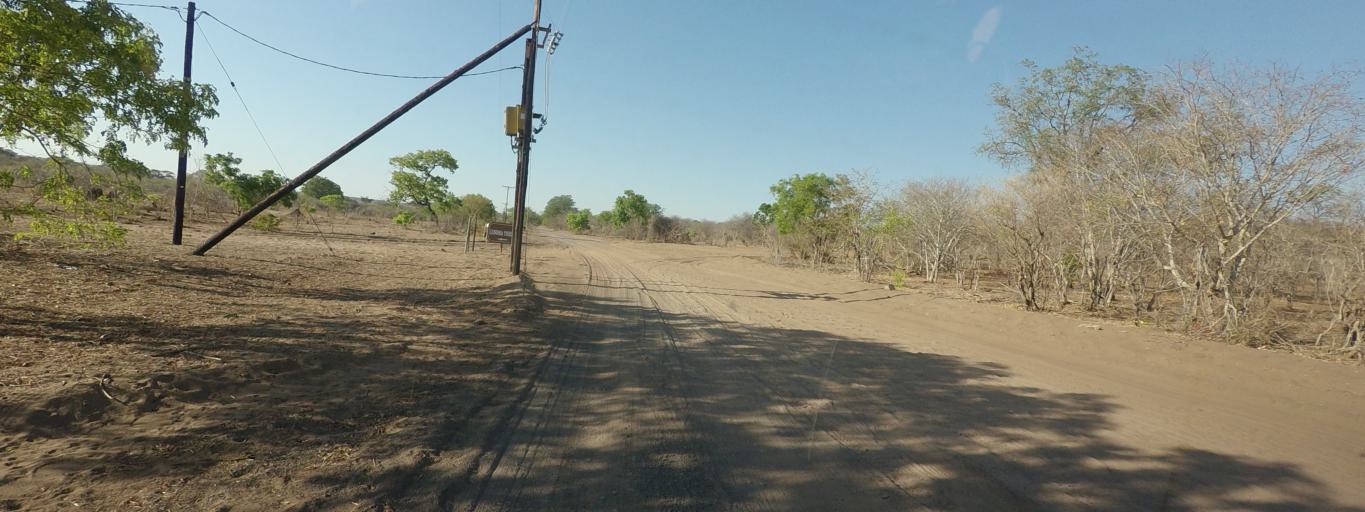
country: BW
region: North West
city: Kasane
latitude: -17.8893
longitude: 25.2295
